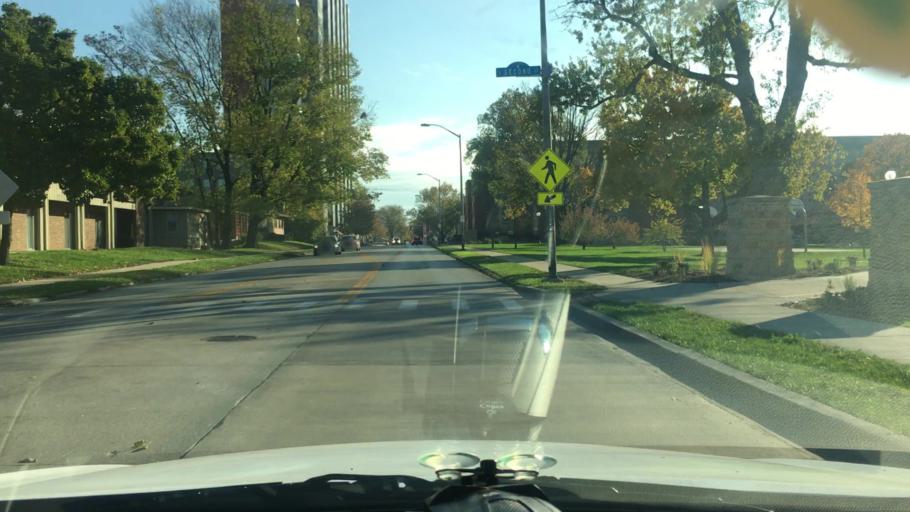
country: US
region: Illinois
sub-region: Champaign County
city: Champaign
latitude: 40.1126
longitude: -88.2371
